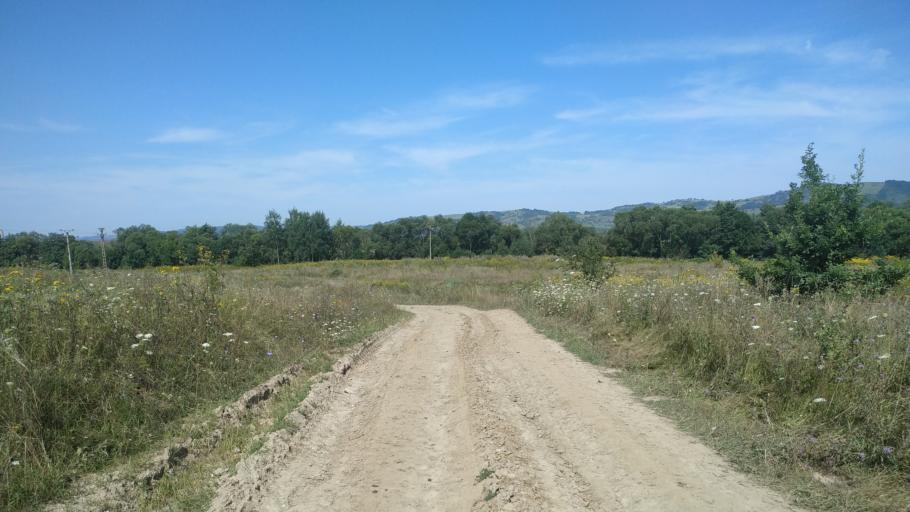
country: RO
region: Brasov
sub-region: Comuna Beclean
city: Beclean
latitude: 45.8253
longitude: 24.9224
